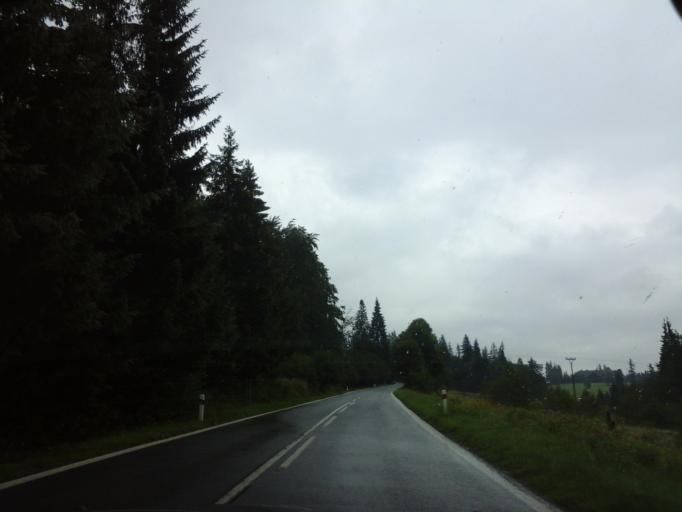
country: PL
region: Lesser Poland Voivodeship
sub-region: Powiat tatrzanski
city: Bukowina Tatrzanska
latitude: 49.2665
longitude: 20.1403
